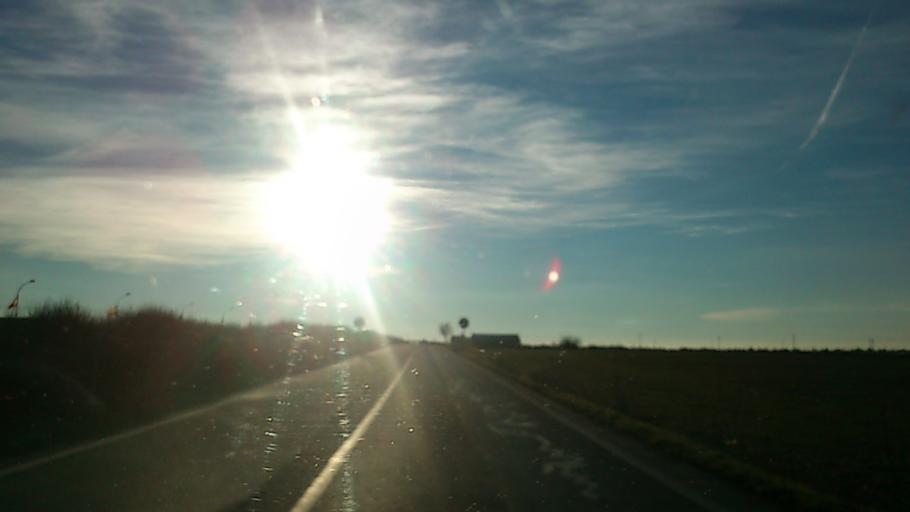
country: ES
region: Castille-La Mancha
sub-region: Provincia de Guadalajara
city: Almadrones
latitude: 40.8952
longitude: -2.7638
